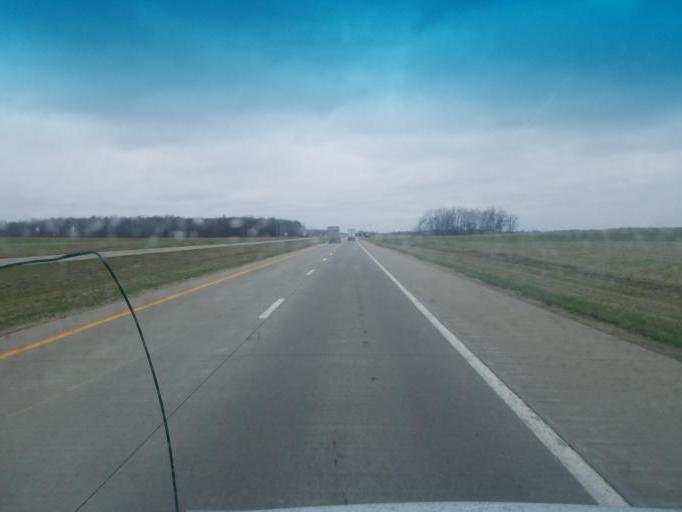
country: US
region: Ohio
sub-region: Hardin County
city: Ada
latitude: 40.8276
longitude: -83.8249
